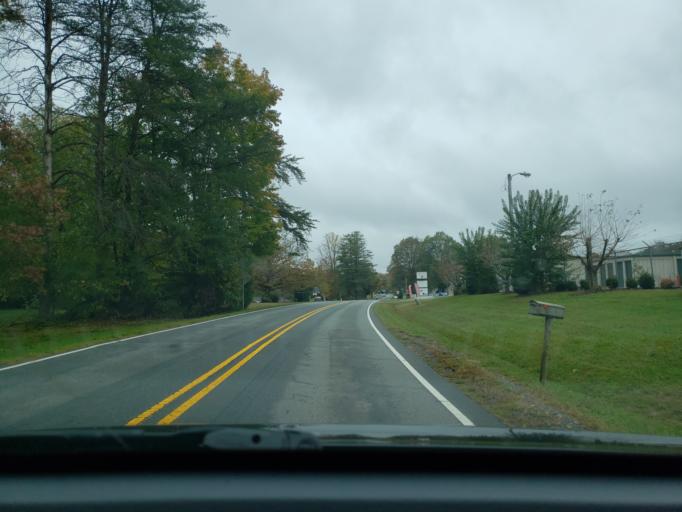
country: US
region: North Carolina
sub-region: Stokes County
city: Walnut Cove
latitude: 36.3247
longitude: -80.1440
